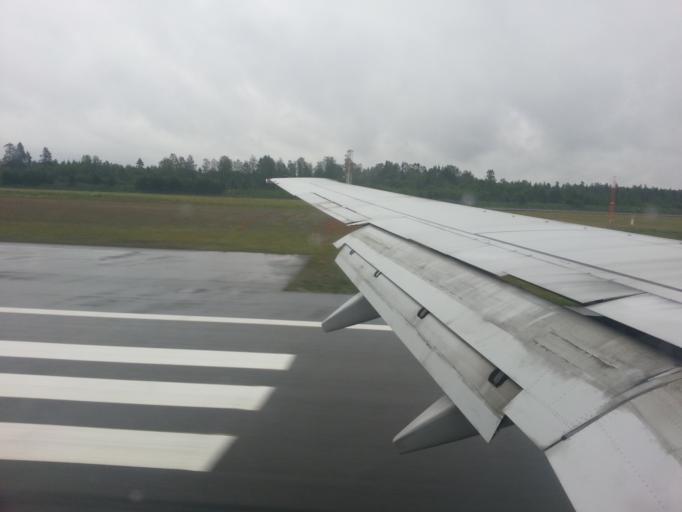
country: NO
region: Akershus
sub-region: Ullensaker
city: Jessheim
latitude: 60.1983
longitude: 11.1208
